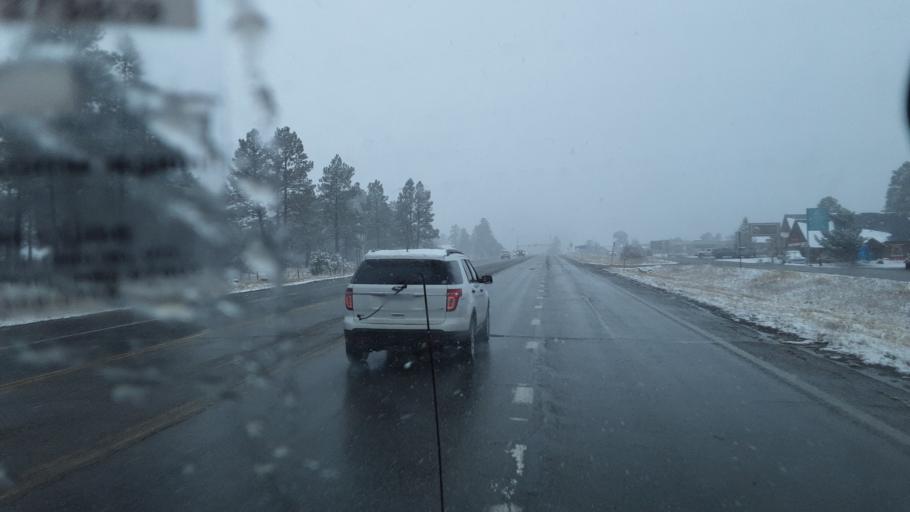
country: US
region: Colorado
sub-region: Archuleta County
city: Pagosa Springs
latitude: 37.2690
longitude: -107.0480
